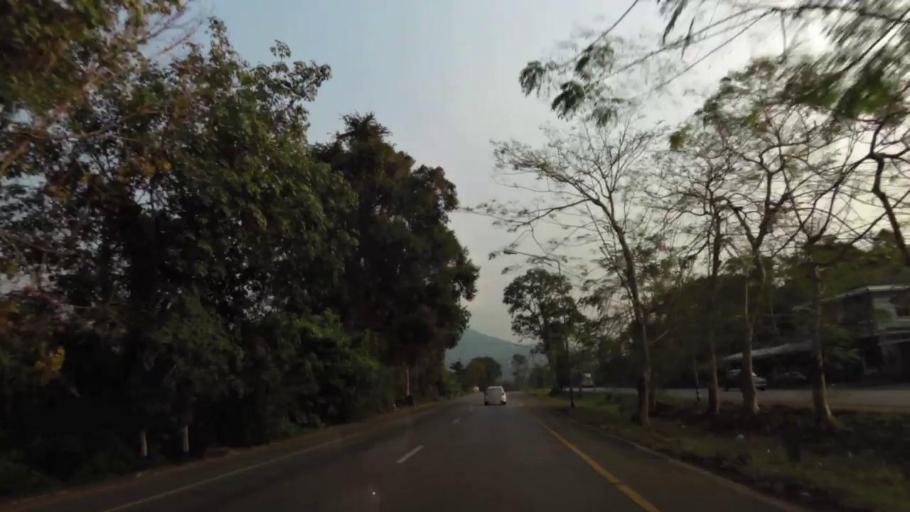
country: TH
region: Chanthaburi
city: Chanthaburi
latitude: 12.5852
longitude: 102.1568
